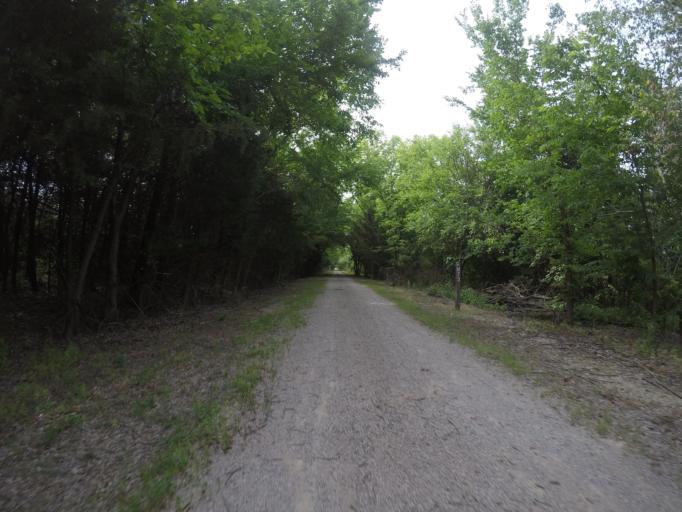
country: US
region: Kansas
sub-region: Anderson County
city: Garnett
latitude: 38.4076
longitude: -95.2598
